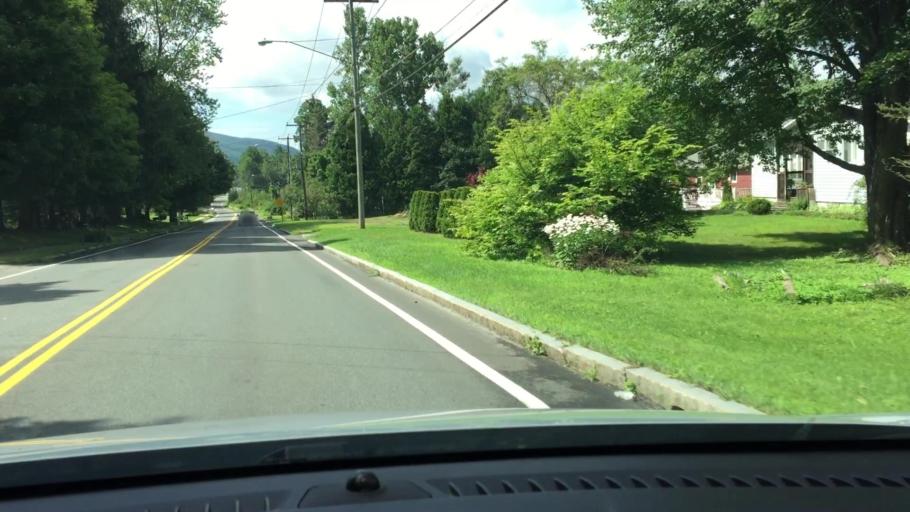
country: US
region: Massachusetts
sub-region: Berkshire County
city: Pittsfield
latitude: 42.4501
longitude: -73.2994
